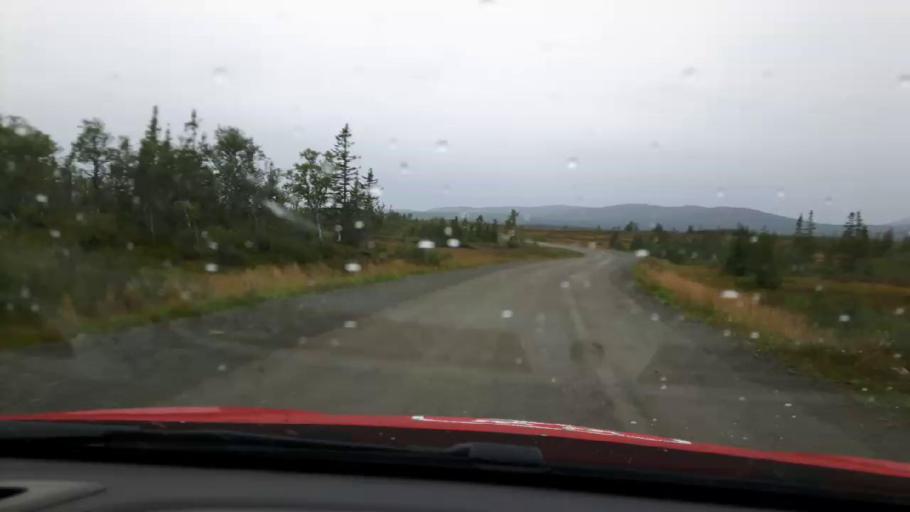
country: NO
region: Nord-Trondelag
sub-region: Meraker
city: Meraker
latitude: 63.5930
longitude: 12.2712
